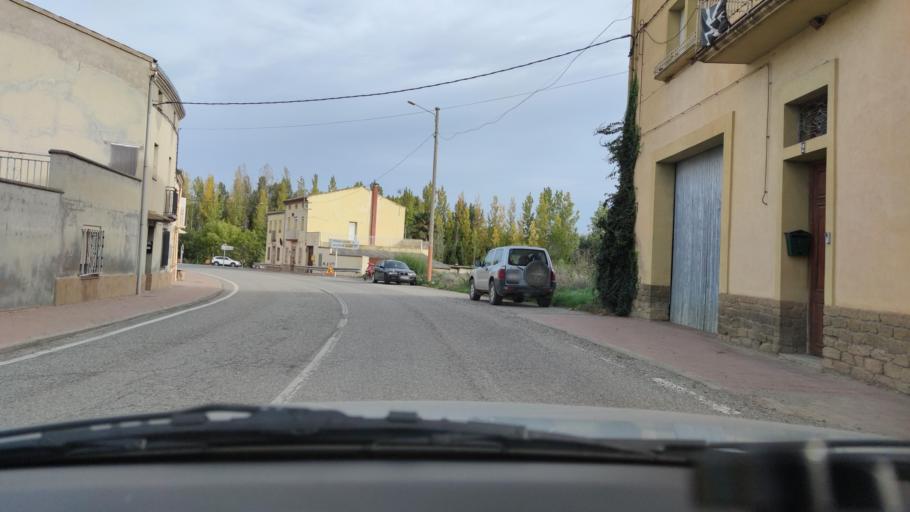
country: ES
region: Catalonia
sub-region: Provincia de Lleida
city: Artesa de Segre
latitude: 41.9074
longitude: 1.0698
